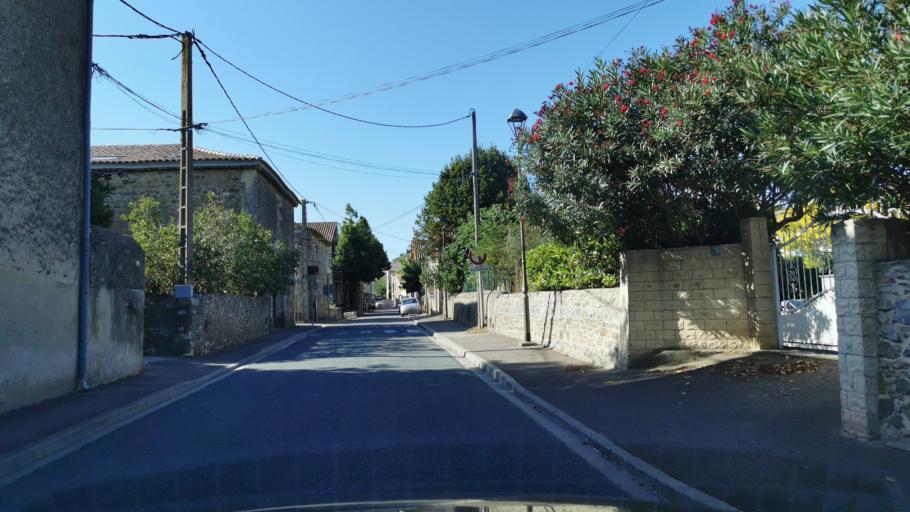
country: FR
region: Languedoc-Roussillon
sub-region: Departement de l'Aude
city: Ginestas
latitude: 43.2745
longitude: 2.8426
